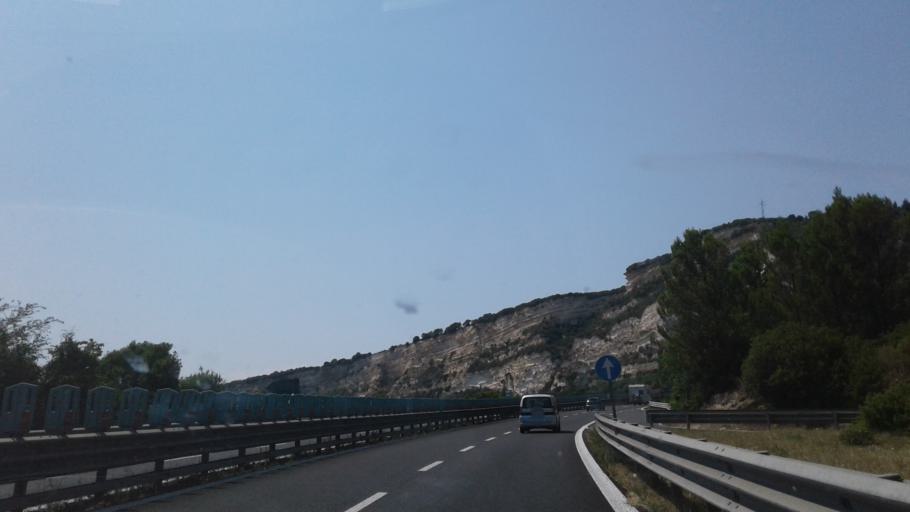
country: IT
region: Sardinia
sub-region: Provincia di Sassari
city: Ossi
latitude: 40.6991
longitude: 8.5939
